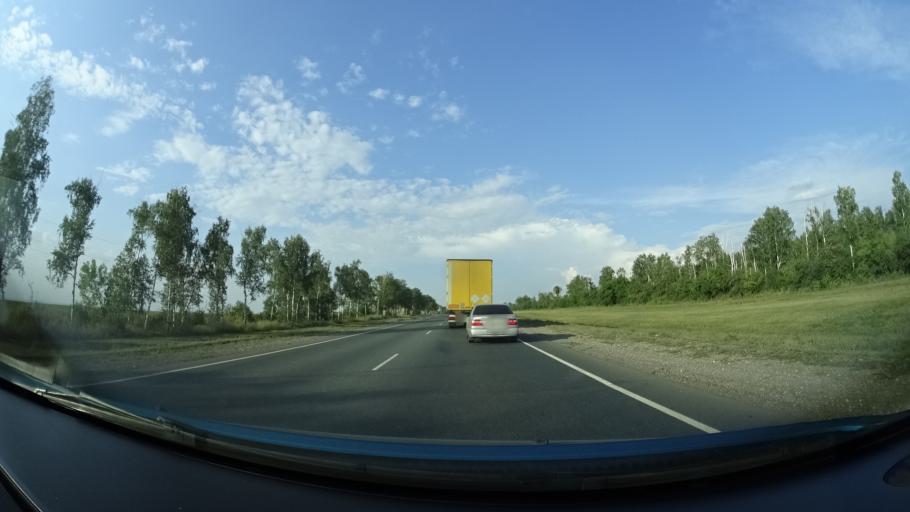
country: RU
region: Samara
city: Krasnyy Yar
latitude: 53.6642
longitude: 50.7585
